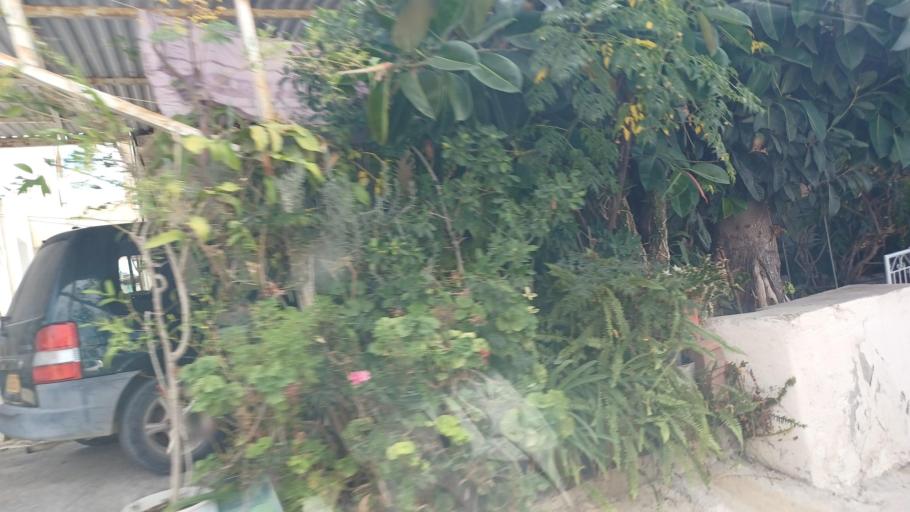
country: CY
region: Pafos
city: Mesogi
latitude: 34.8099
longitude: 32.4627
